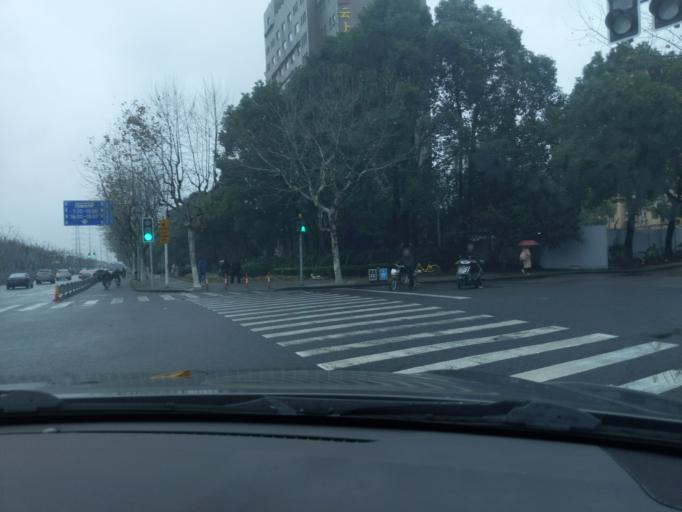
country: CN
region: Shanghai Shi
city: Huamu
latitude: 31.1894
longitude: 121.5246
